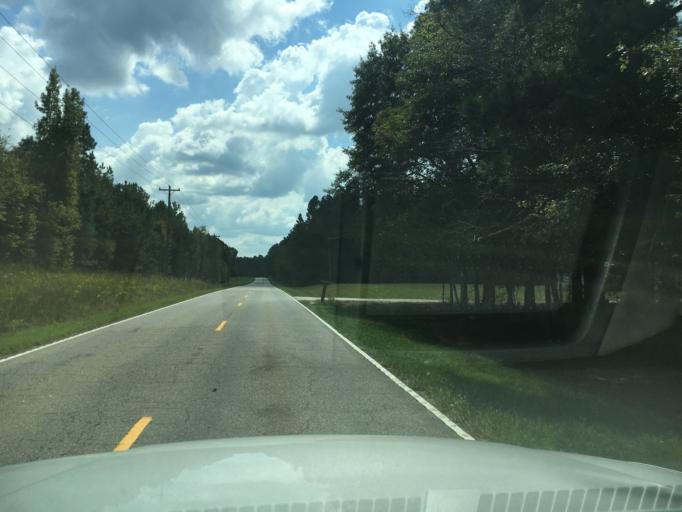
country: US
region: South Carolina
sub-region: Greenwood County
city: Greenwood
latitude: 34.1228
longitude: -82.1267
